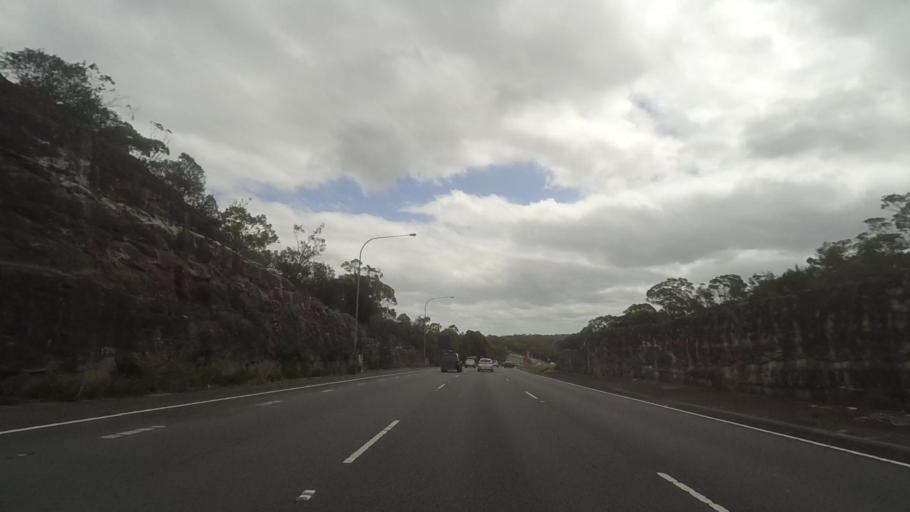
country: AU
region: New South Wales
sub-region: Gosford Shire
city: Point Clare
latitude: -33.4582
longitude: 151.2027
